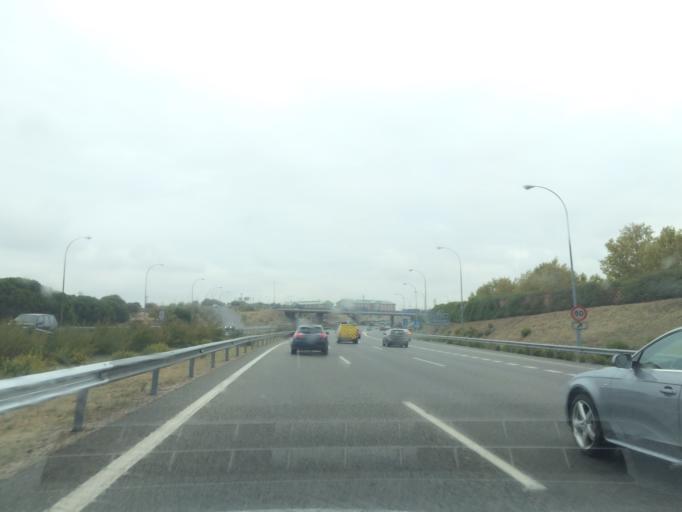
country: ES
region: Madrid
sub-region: Provincia de Madrid
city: Pozuelo de Alarcon
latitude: 40.4560
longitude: -3.8154
